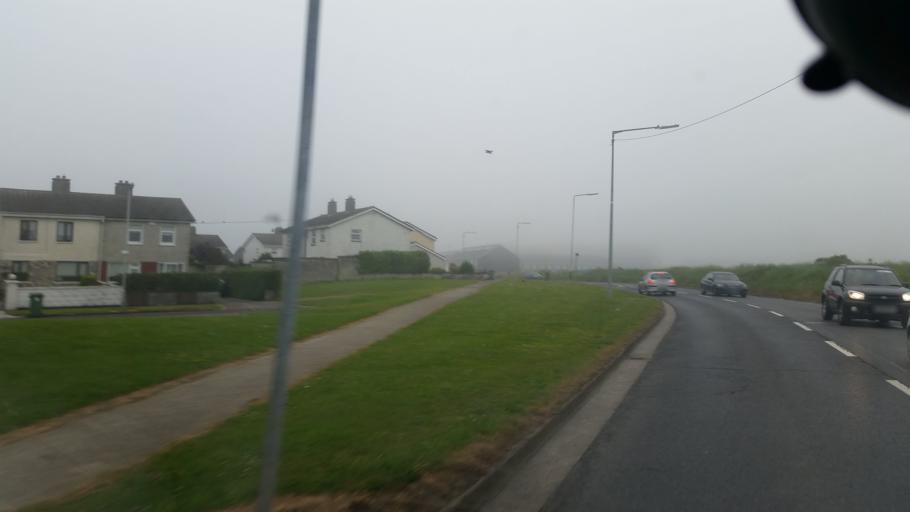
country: IE
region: Leinster
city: Ballymun
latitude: 53.4048
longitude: -6.2776
